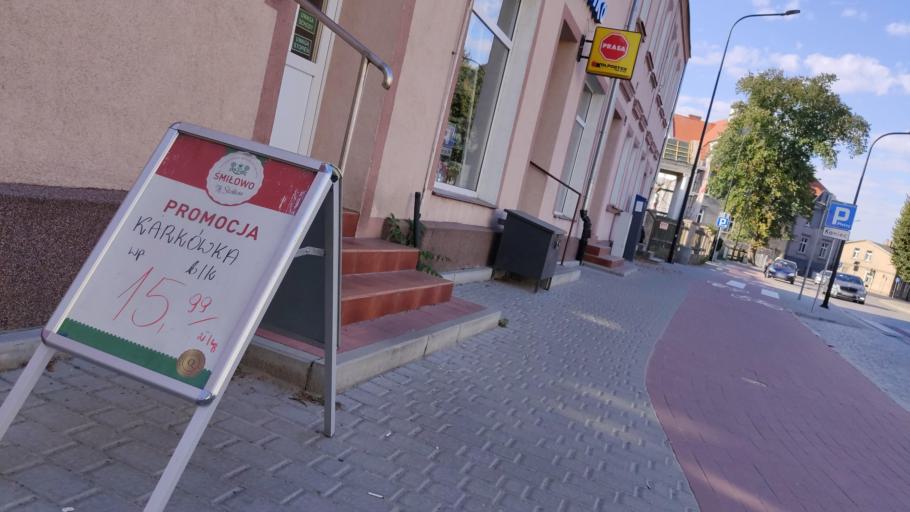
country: PL
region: Kujawsko-Pomorskie
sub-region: Powiat zninski
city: Znin
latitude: 52.8472
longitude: 17.7293
